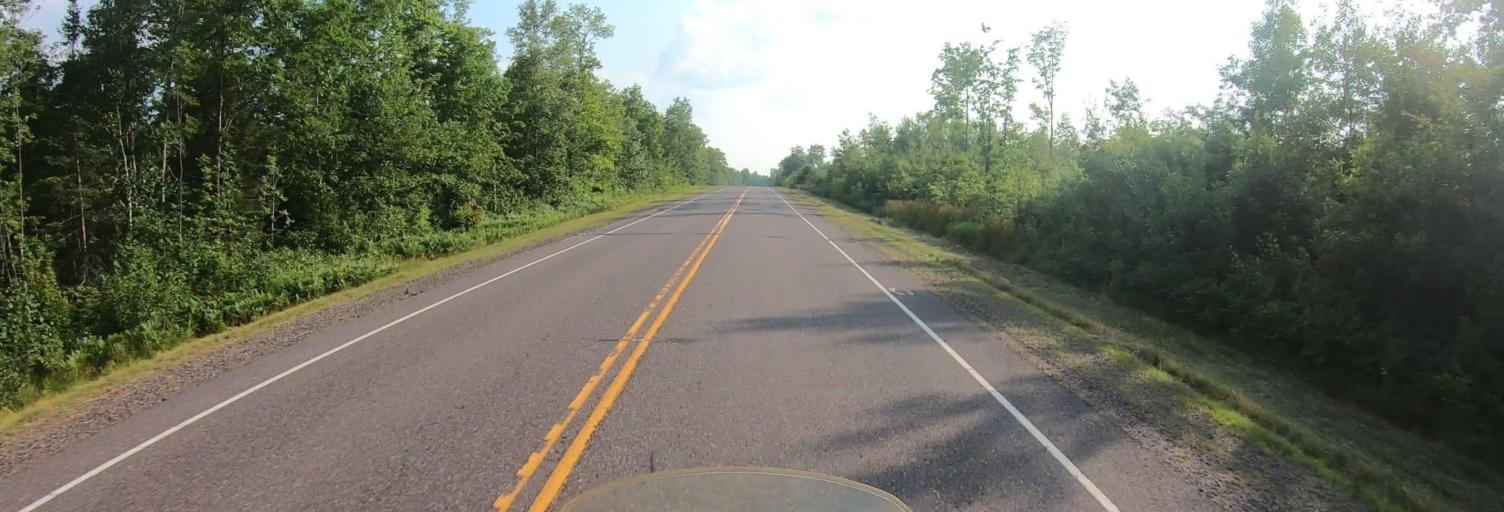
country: US
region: Wisconsin
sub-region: Sawyer County
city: Little Round Lake
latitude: 46.0803
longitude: -91.0193
